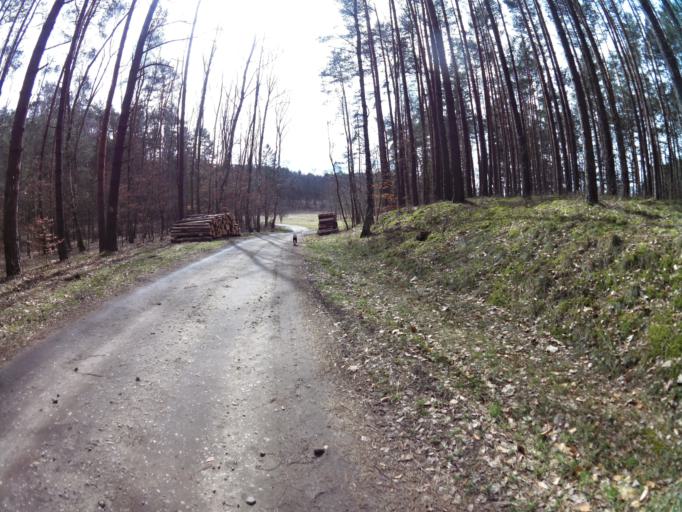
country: PL
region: West Pomeranian Voivodeship
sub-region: Powiat mysliborski
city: Mysliborz
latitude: 52.8540
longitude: 14.8405
